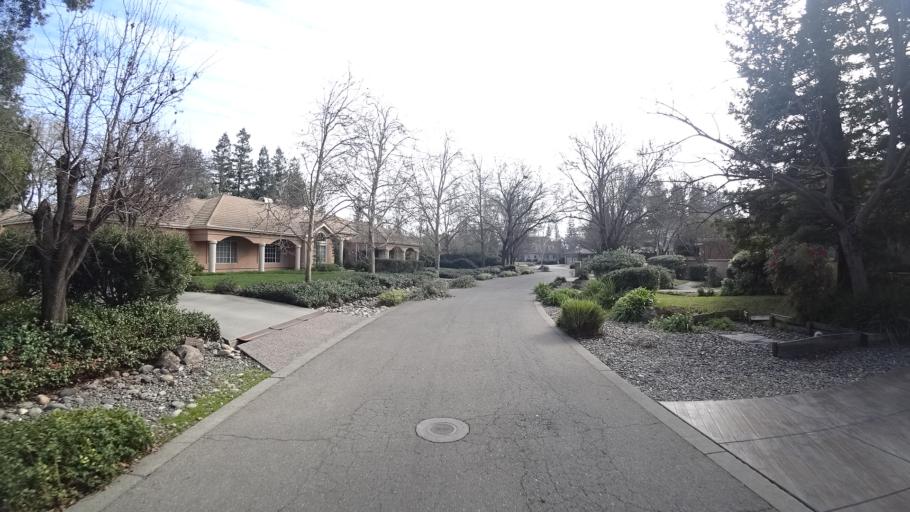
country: US
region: California
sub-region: Yolo County
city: Davis
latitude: 38.5386
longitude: -121.7165
